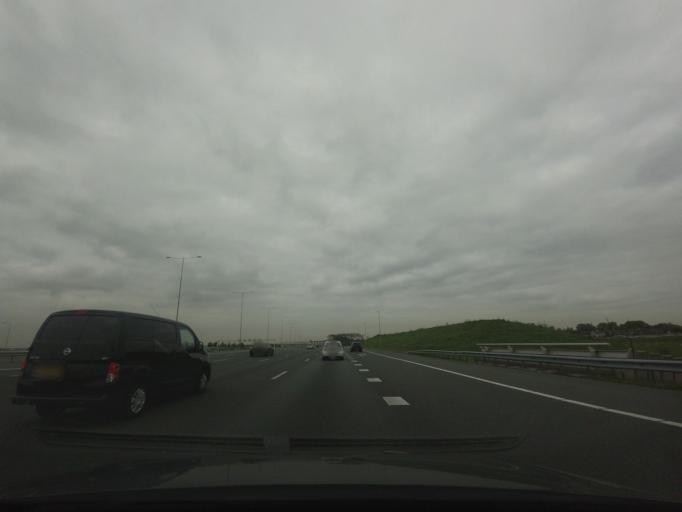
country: NL
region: North Holland
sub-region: Gemeente Amsterdam
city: Amsterdam-Zuidoost
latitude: 52.2610
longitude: 4.9652
